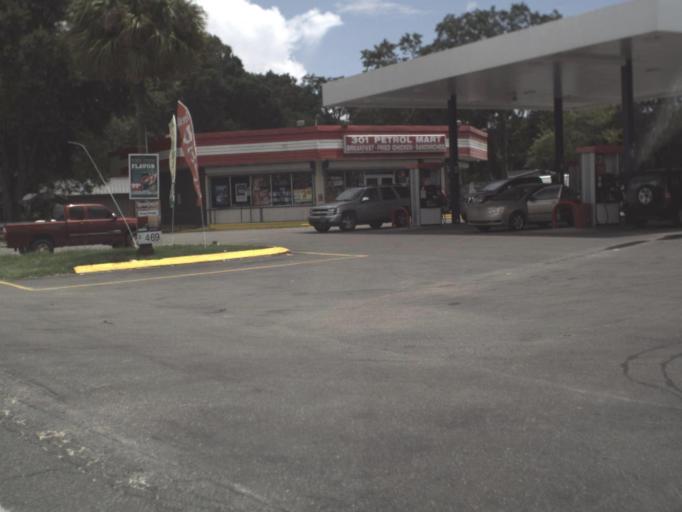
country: US
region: Florida
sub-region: Hillsborough County
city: Thonotosassa
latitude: 28.0548
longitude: -82.3283
